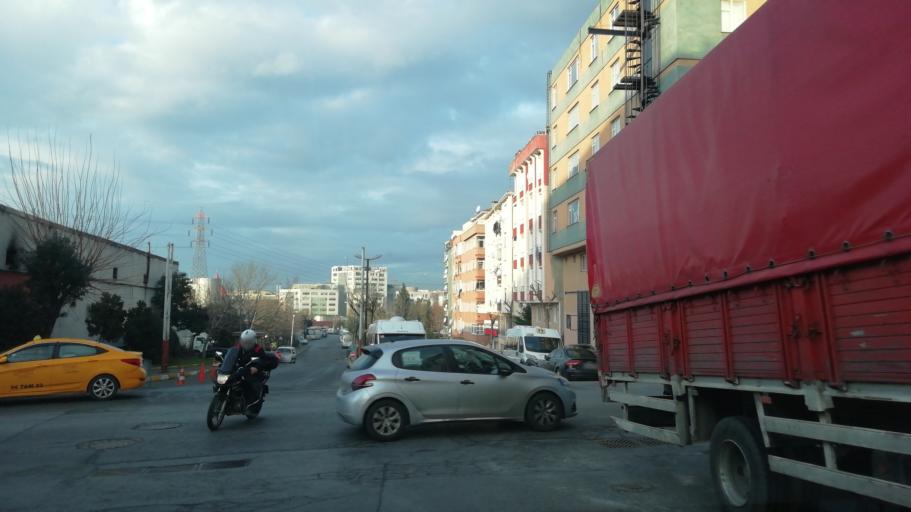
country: TR
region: Istanbul
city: Bahcelievler
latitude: 40.9994
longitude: 28.8273
